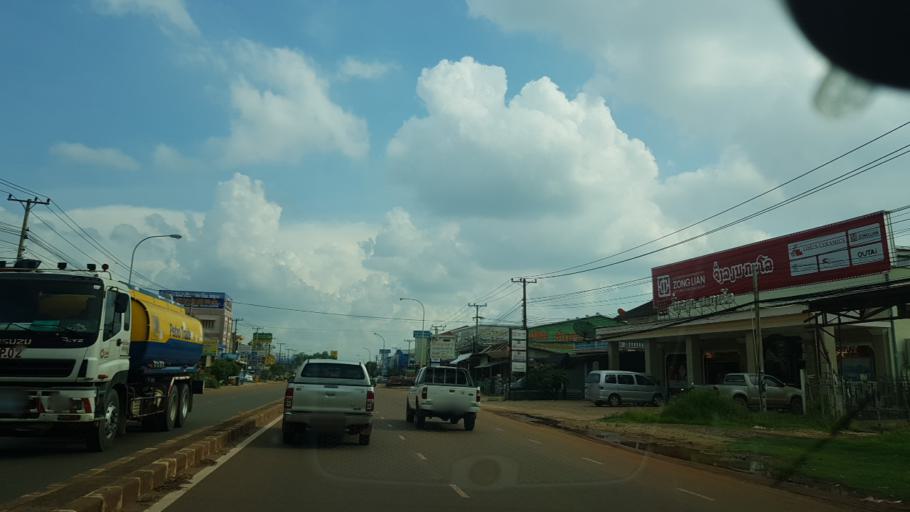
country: LA
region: Vientiane
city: Vientiane
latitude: 18.0226
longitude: 102.6515
